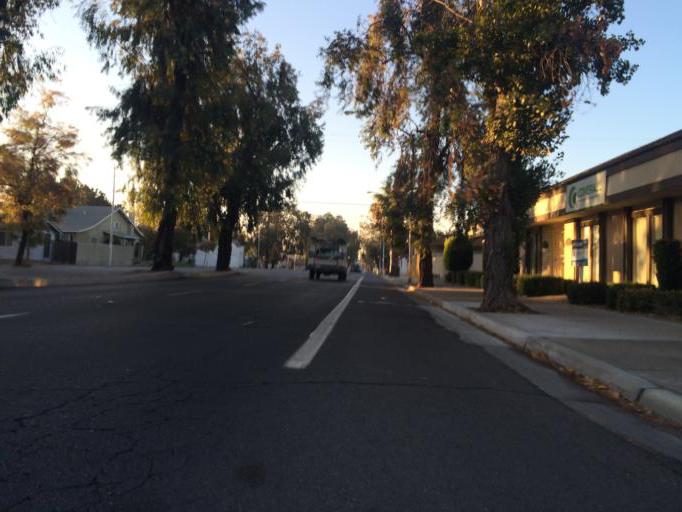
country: US
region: California
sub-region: Fresno County
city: Fresno
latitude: 36.7486
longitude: -119.7726
